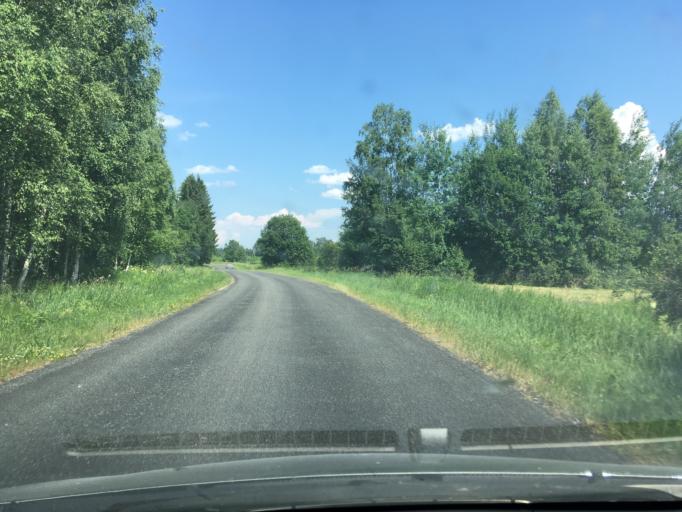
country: EE
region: Raplamaa
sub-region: Maerjamaa vald
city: Marjamaa
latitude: 58.7586
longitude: 24.4157
